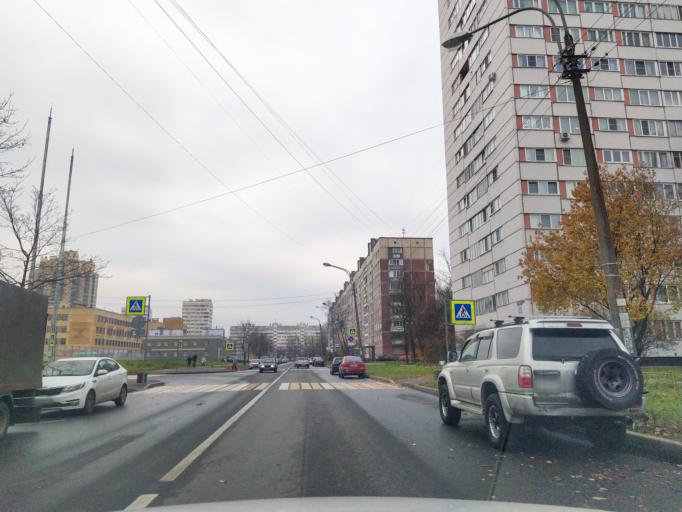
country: RU
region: St.-Petersburg
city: Sosnovka
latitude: 60.0421
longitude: 30.3556
